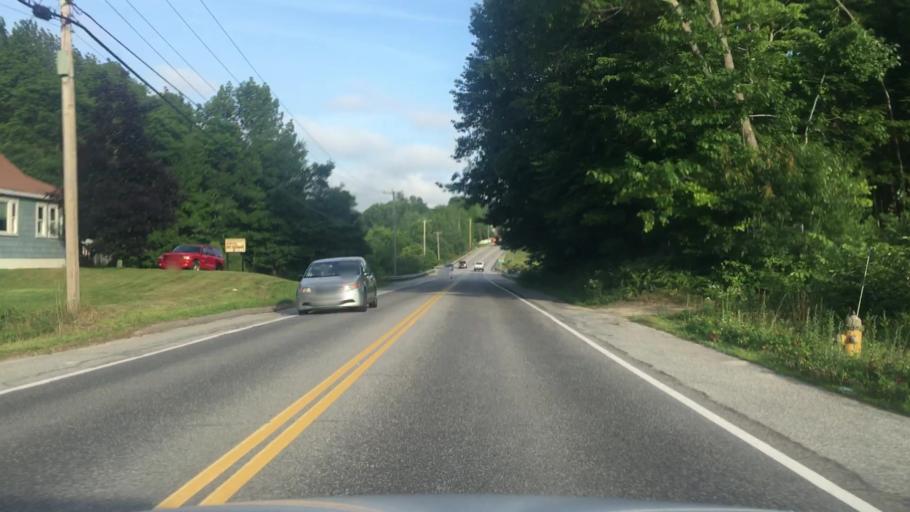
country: US
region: Maine
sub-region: Cumberland County
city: North Windham
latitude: 43.8069
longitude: -70.4118
